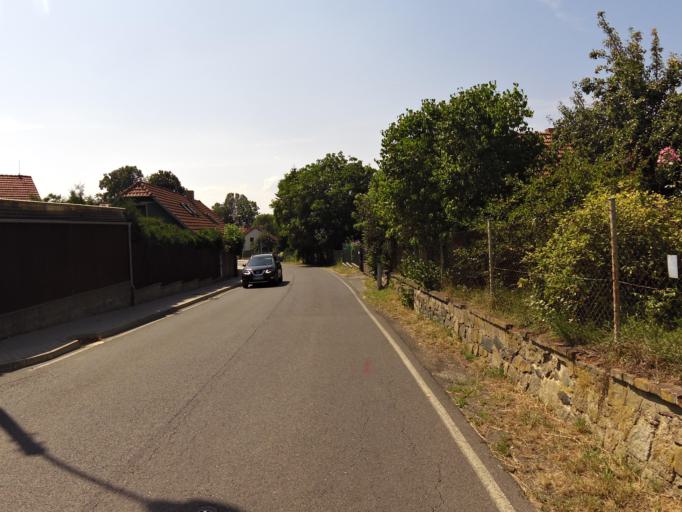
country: CZ
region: Central Bohemia
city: Mukarov
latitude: 49.9535
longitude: 14.7459
